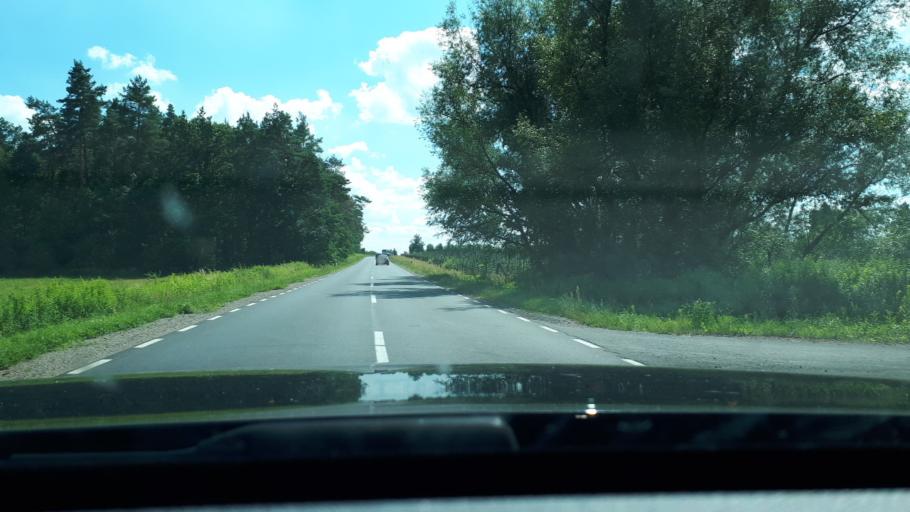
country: PL
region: Masovian Voivodeship
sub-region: Powiat grojecki
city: Warka
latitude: 51.8661
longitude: 21.2140
